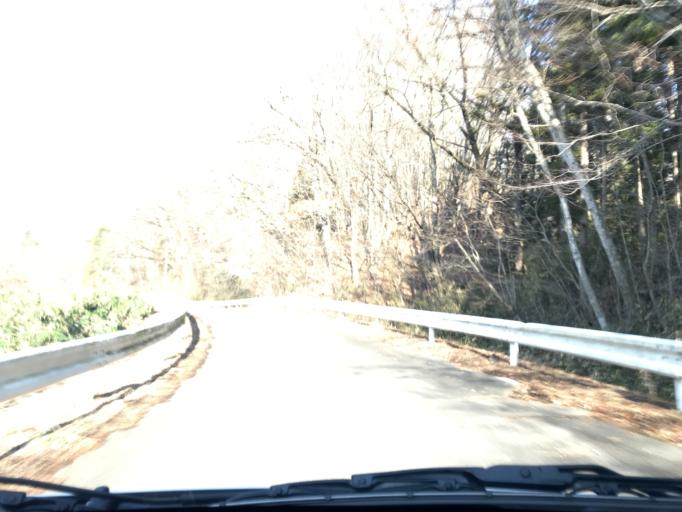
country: JP
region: Iwate
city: Ichinoseki
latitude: 38.9701
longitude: 141.0430
